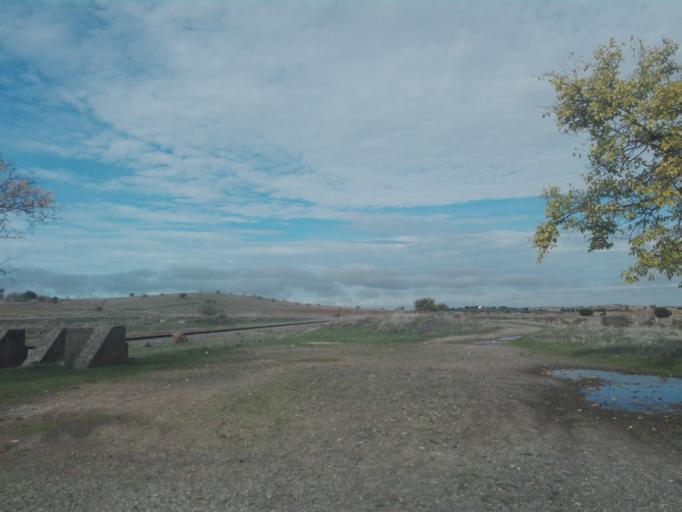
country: ES
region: Extremadura
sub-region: Provincia de Badajoz
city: Villagarcia de la Torre
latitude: 38.2859
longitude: -6.0942
